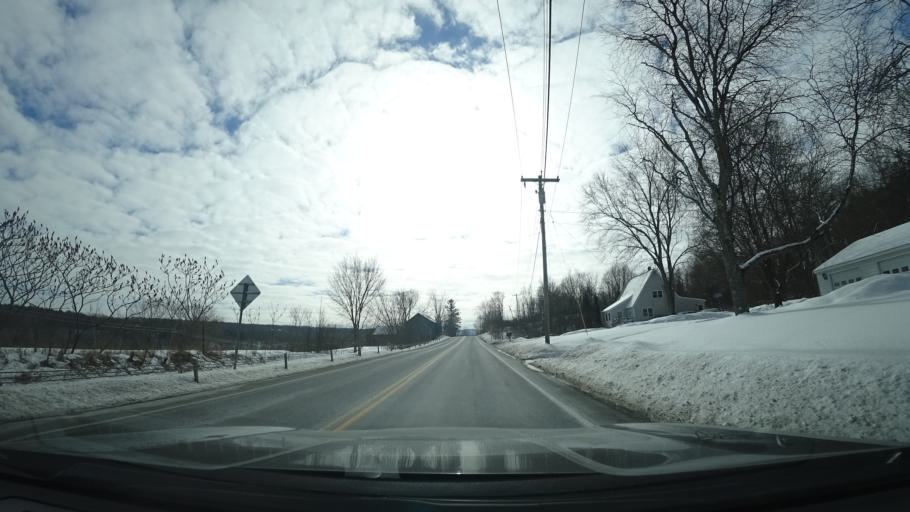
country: US
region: New York
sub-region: Washington County
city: Fort Edward
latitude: 43.2590
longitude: -73.5113
